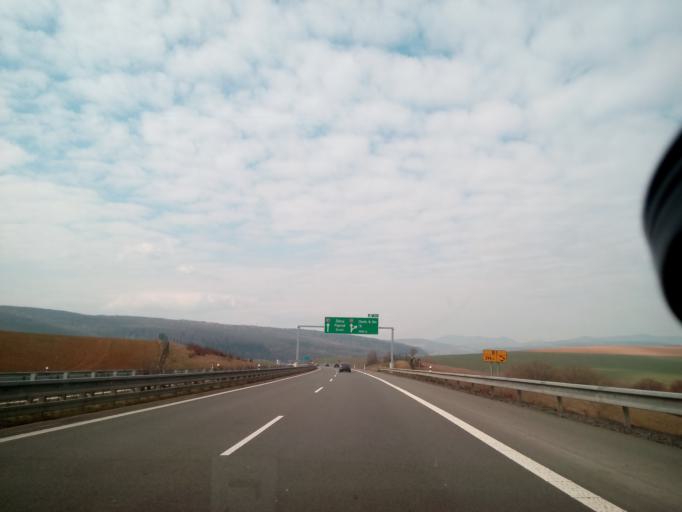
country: SK
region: Presovsky
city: Sabinov
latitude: 49.0069
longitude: 21.1253
